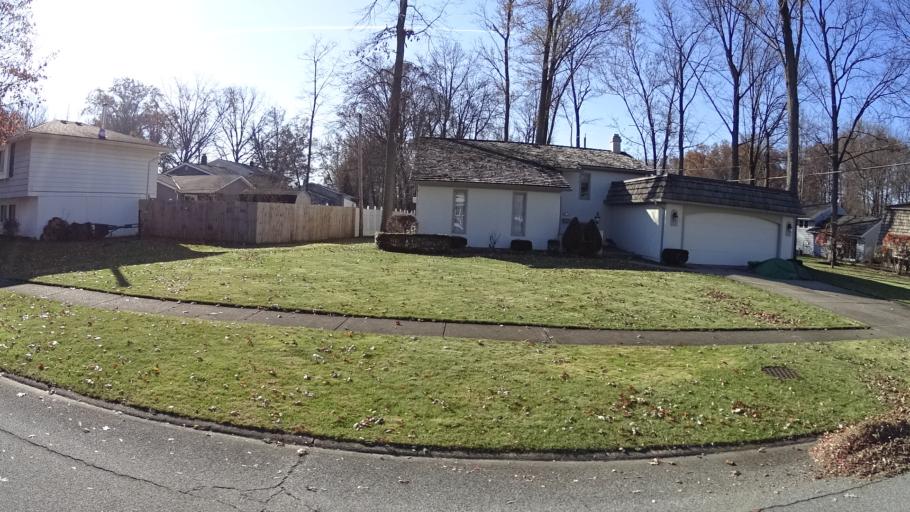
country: US
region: Ohio
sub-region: Lorain County
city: Sheffield
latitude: 41.3927
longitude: -82.0727
